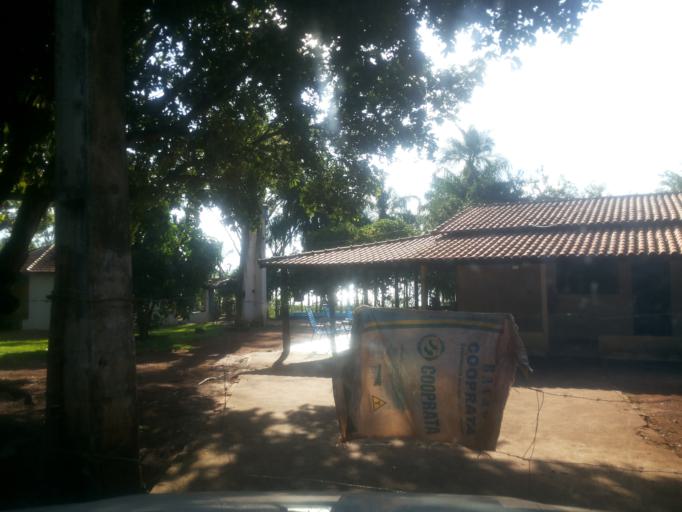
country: BR
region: Minas Gerais
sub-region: Santa Vitoria
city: Santa Vitoria
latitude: -18.9875
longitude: -50.3717
